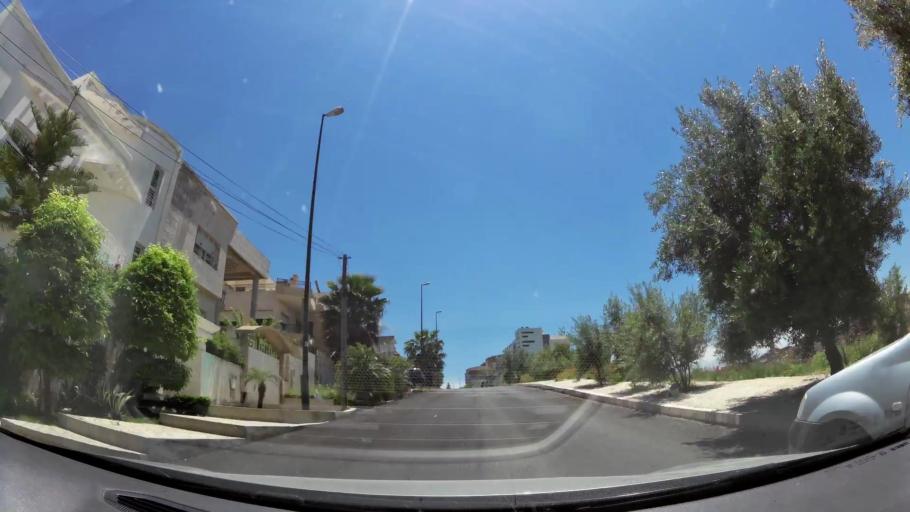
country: MA
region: Meknes-Tafilalet
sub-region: Meknes
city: Meknes
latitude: 33.9114
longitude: -5.5542
